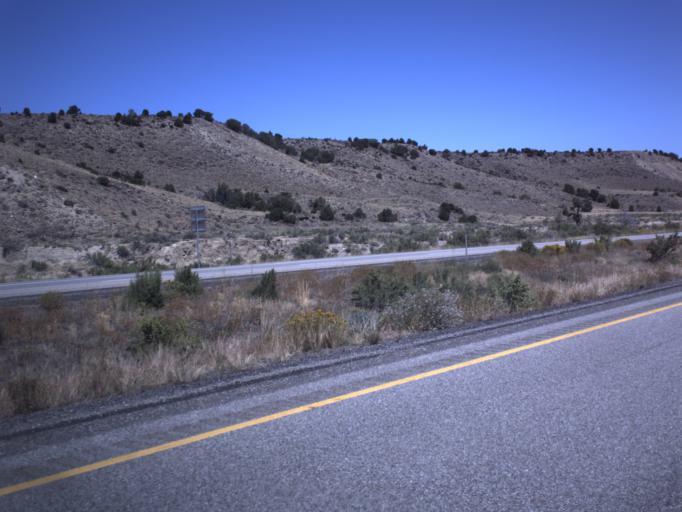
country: US
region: Utah
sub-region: Emery County
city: Ferron
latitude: 38.7617
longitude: -111.3649
